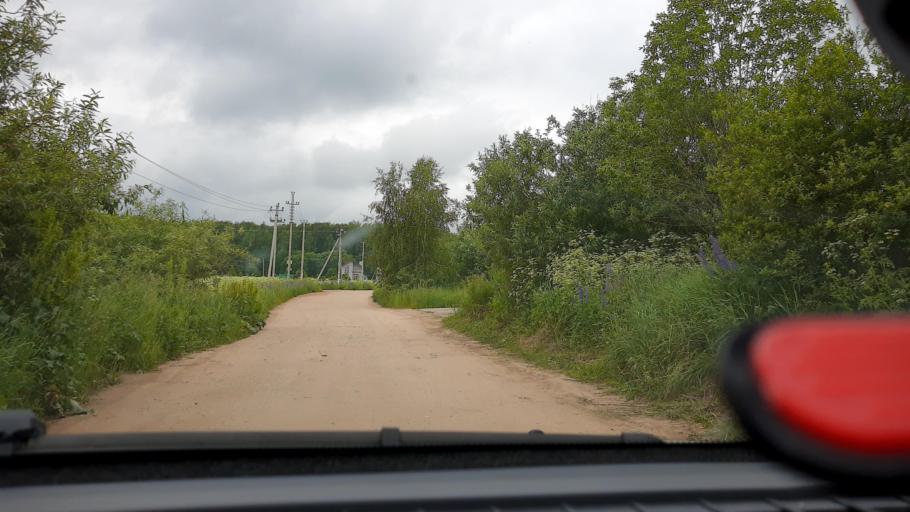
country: RU
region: Nizjnij Novgorod
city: Burevestnik
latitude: 56.1011
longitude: 43.9293
